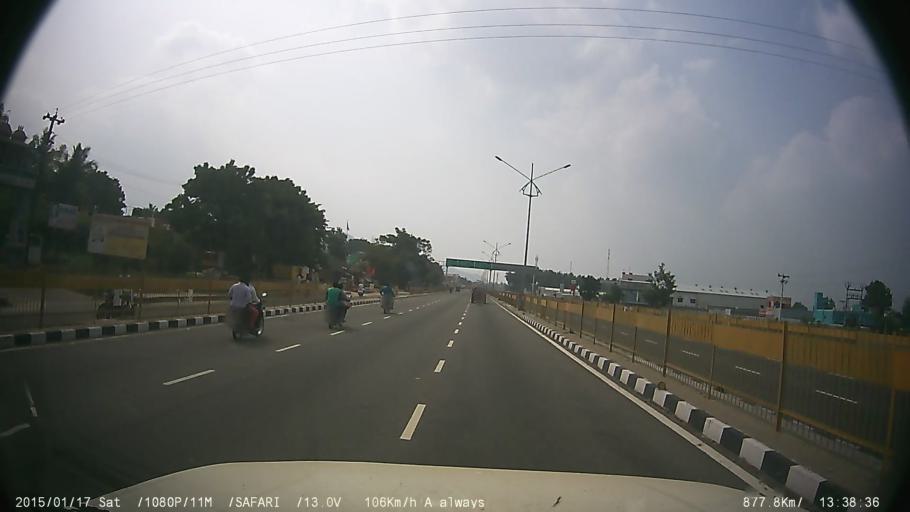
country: IN
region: Tamil Nadu
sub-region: Vellore
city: Katpadi
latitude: 12.9436
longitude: 79.1952
